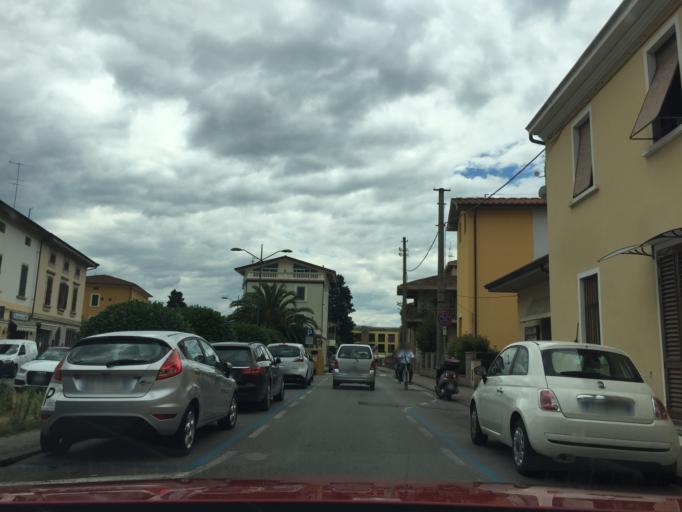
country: IT
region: Tuscany
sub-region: Provincia di Pistoia
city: Montecatini-Terme
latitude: 43.8797
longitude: 10.7753
